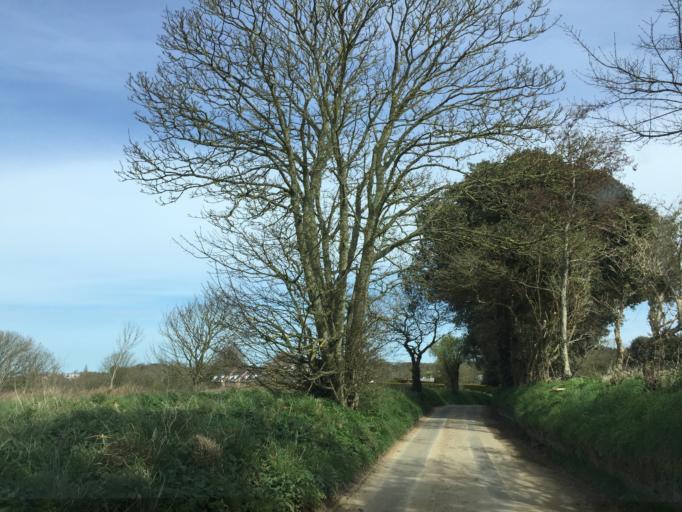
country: JE
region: St Helier
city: Saint Helier
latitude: 49.2378
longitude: -2.1839
